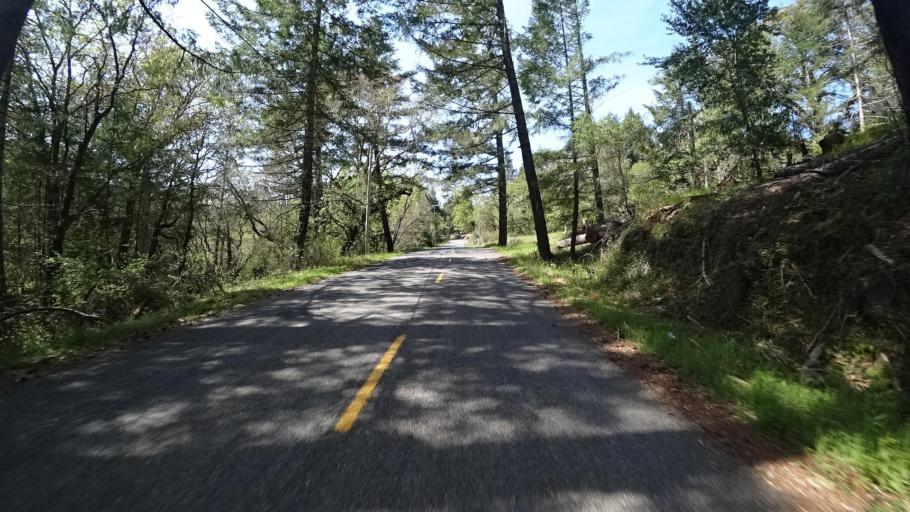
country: US
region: California
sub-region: Humboldt County
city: Redway
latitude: 40.3476
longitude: -123.7120
